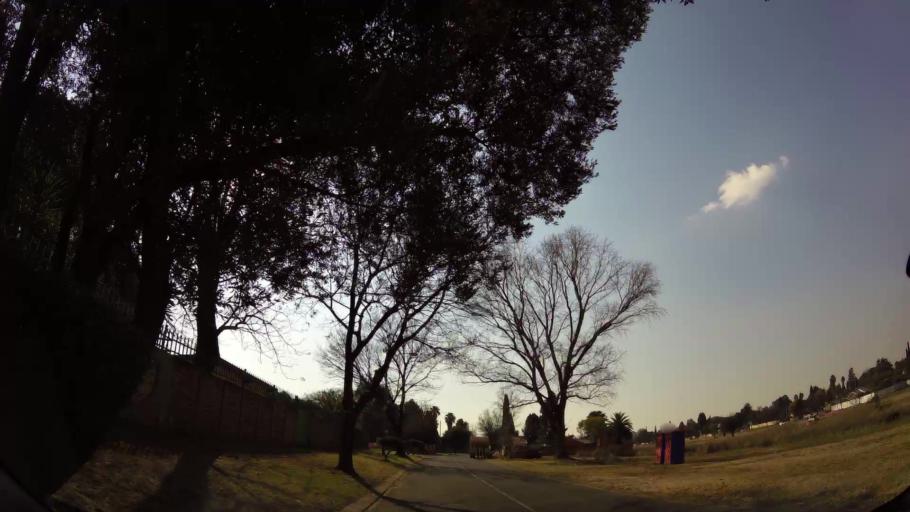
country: ZA
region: Gauteng
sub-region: Ekurhuleni Metropolitan Municipality
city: Benoni
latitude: -26.1526
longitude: 28.2877
